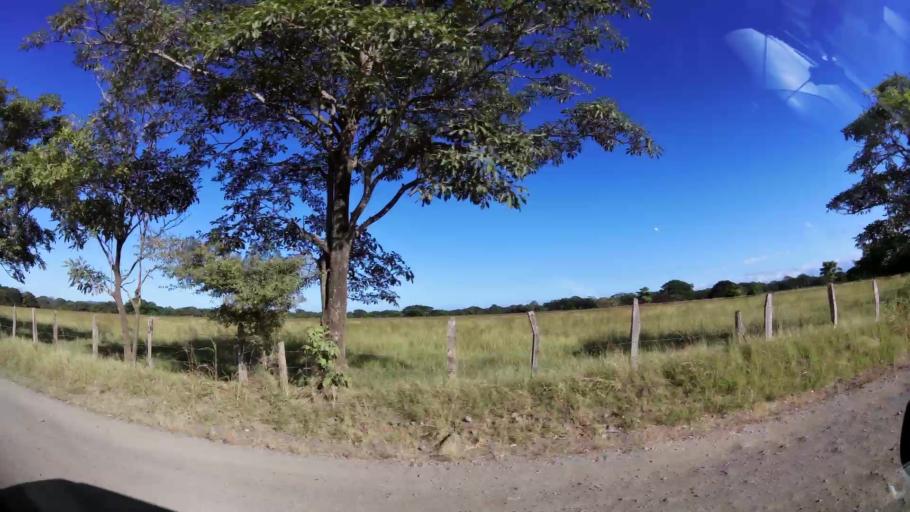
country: CR
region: Guanacaste
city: Sardinal
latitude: 10.4833
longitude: -85.5923
